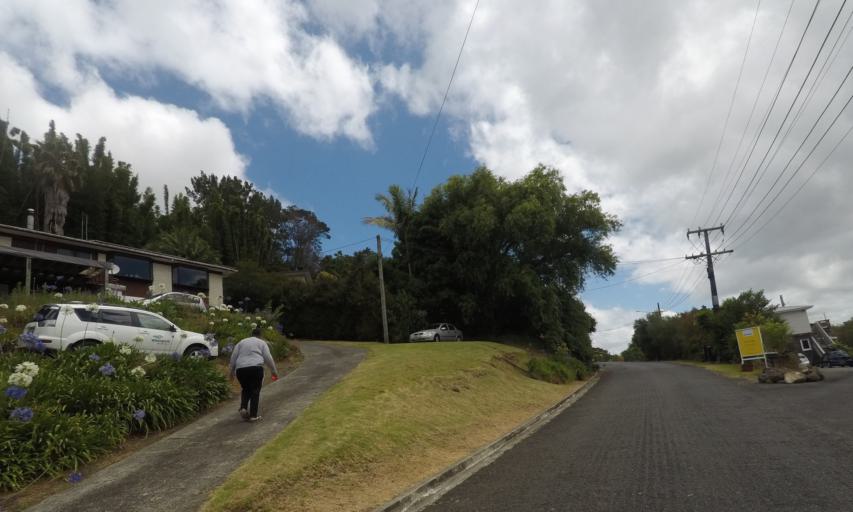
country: NZ
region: Northland
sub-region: Whangarei
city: Whangarei
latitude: -35.7424
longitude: 174.3617
